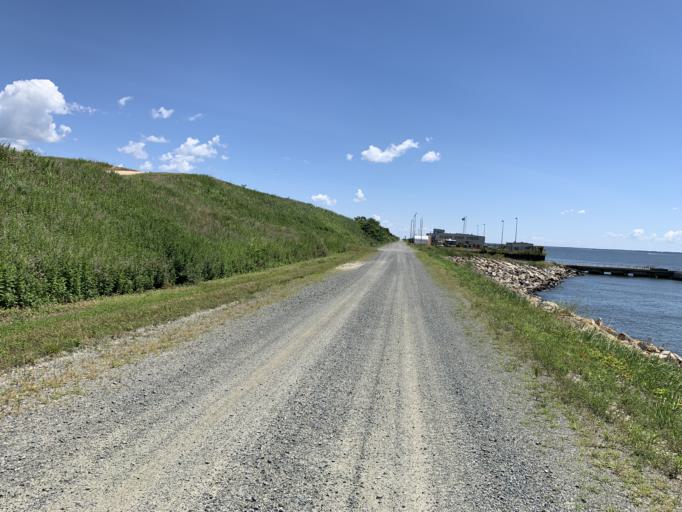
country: US
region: Maryland
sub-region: Baltimore County
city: Edgemere
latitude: 39.2405
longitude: -76.3664
